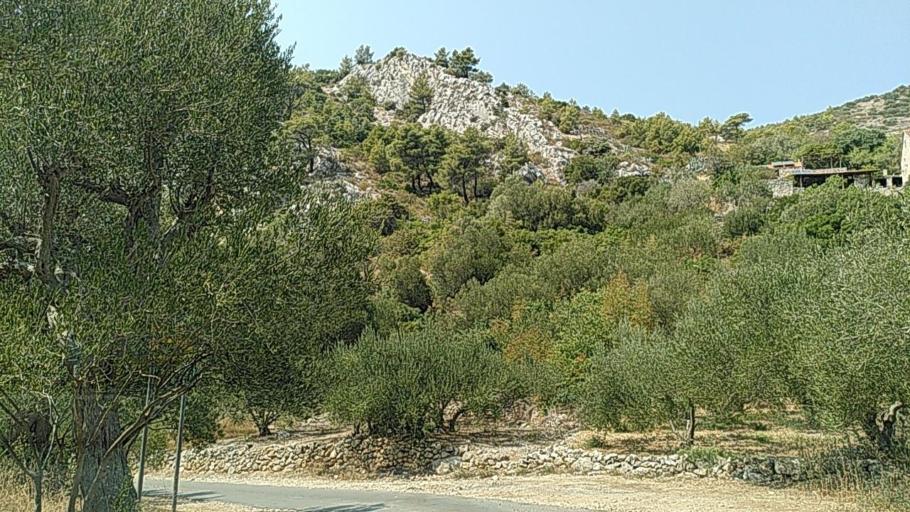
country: HR
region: Splitsko-Dalmatinska
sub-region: Grad Hvar
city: Hvar
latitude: 43.1680
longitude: 16.5029
